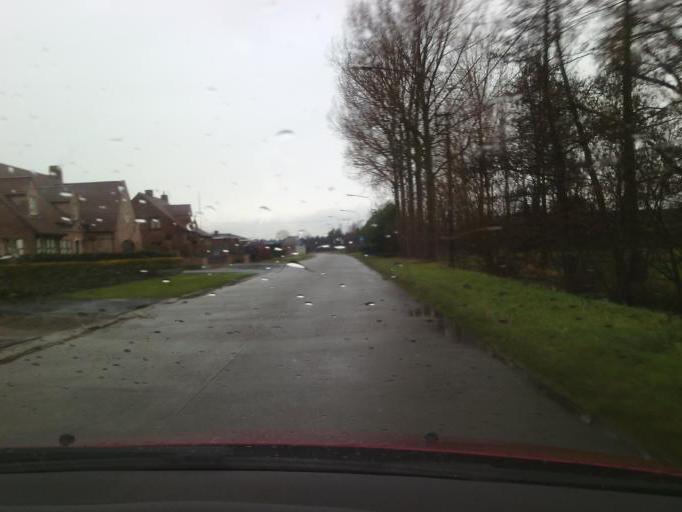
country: BE
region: Flanders
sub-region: Provincie Oost-Vlaanderen
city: Wetteren
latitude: 51.0621
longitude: 3.9130
